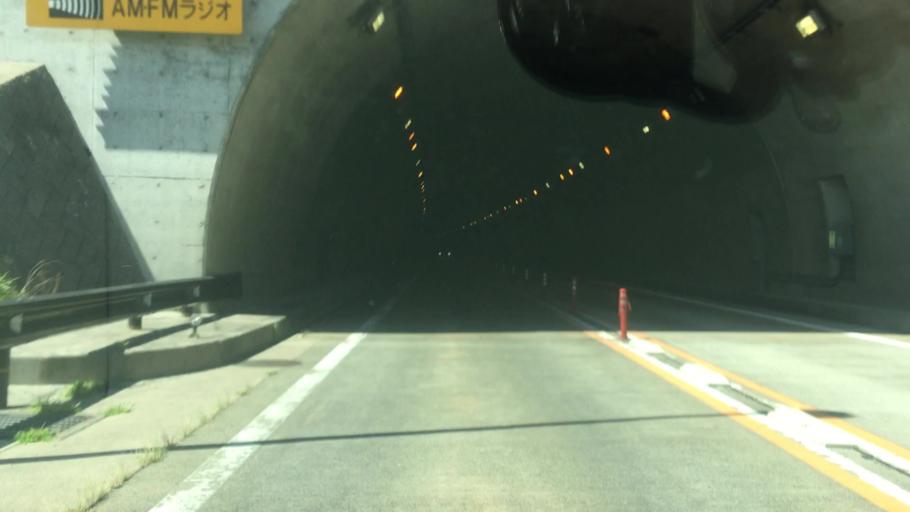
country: JP
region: Tottori
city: Tottori
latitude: 35.3811
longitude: 134.2049
